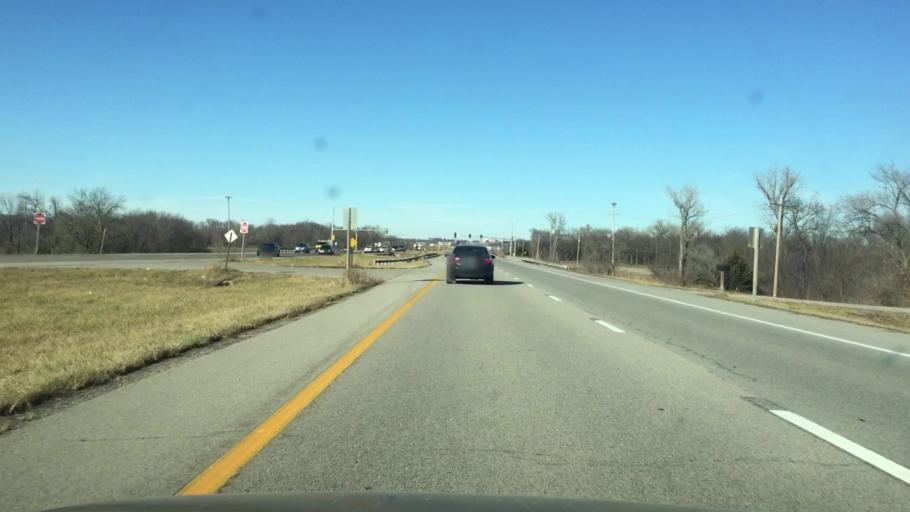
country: US
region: Kansas
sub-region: Douglas County
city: Lawrence
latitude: 38.9062
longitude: -95.2604
